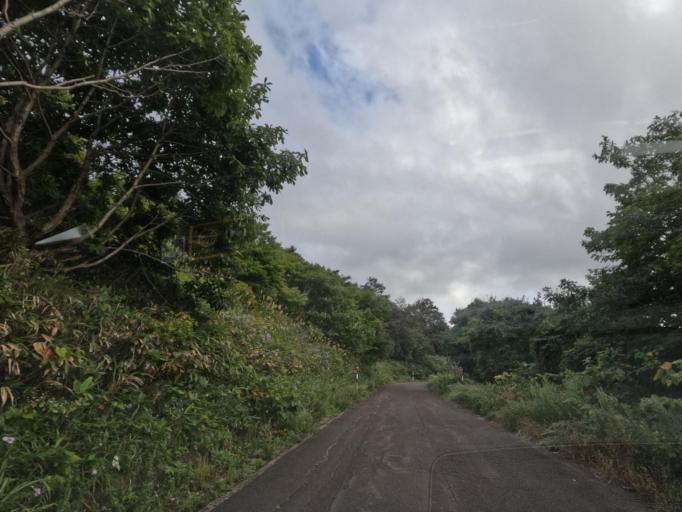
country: JP
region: Hokkaido
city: Muroran
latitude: 42.3305
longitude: 141.0025
